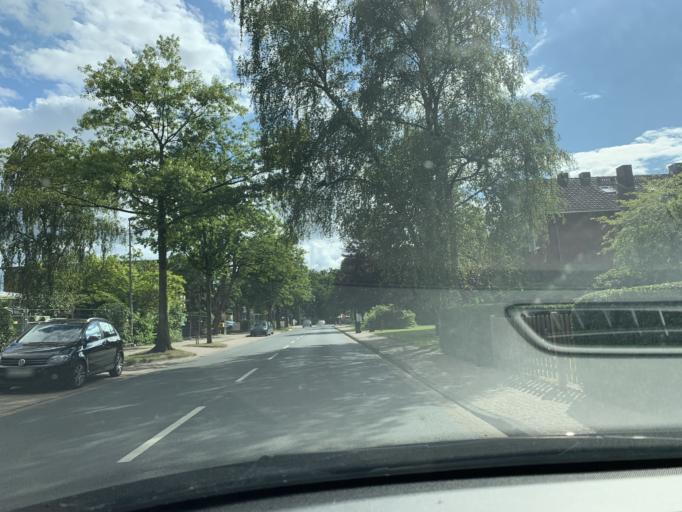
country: DE
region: Lower Saxony
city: Bad Zwischenahn
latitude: 53.1938
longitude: 7.9880
